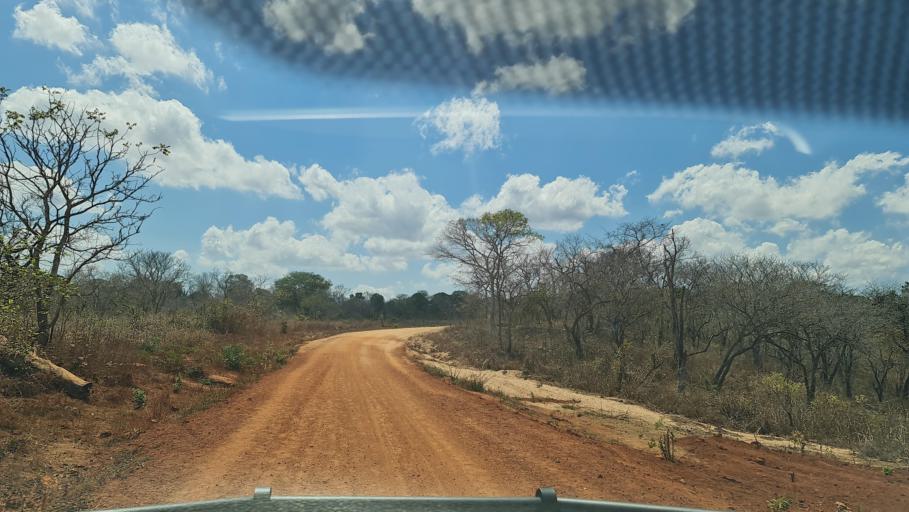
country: MZ
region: Nampula
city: Nacala
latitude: -14.1691
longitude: 40.2532
